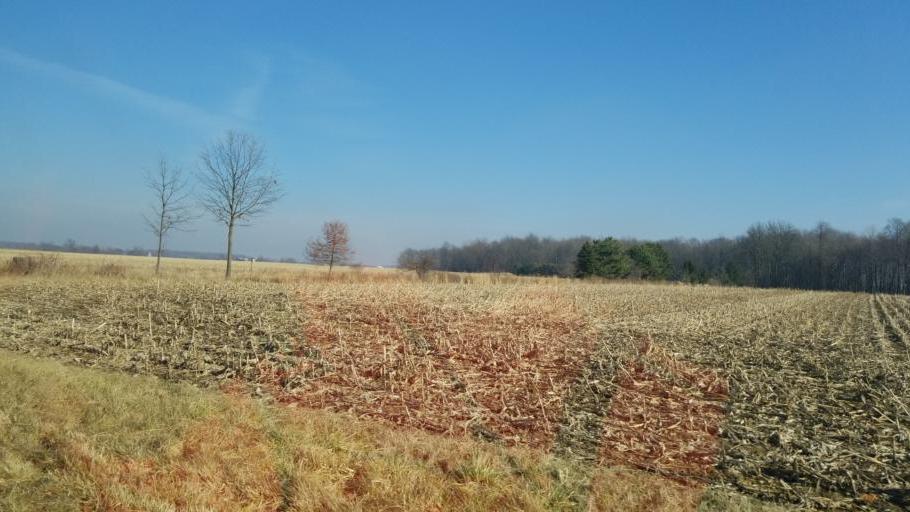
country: US
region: Ohio
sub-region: Seneca County
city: Tiffin
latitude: 40.9793
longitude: -83.0742
